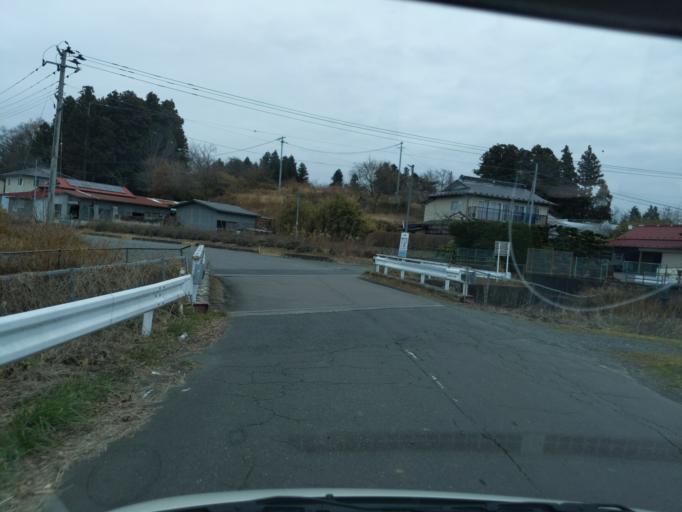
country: JP
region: Iwate
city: Ichinoseki
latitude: 38.7341
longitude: 141.2492
